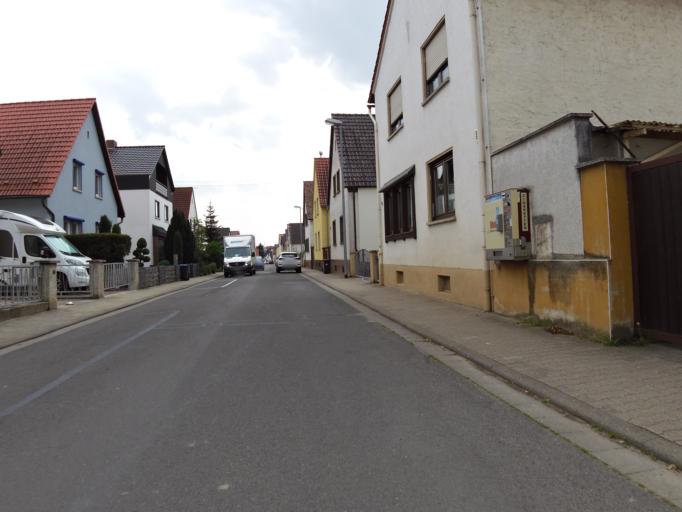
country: DE
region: Rheinland-Pfalz
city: Fussgonheim
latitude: 49.4585
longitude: 8.2916
